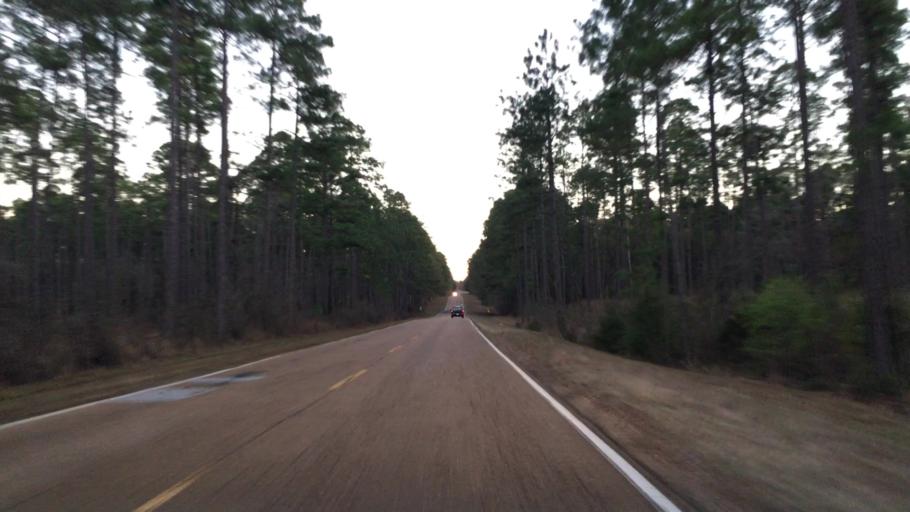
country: US
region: Louisiana
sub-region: Vernon Parish
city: Fort Polk South
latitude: 31.0114
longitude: -93.1865
